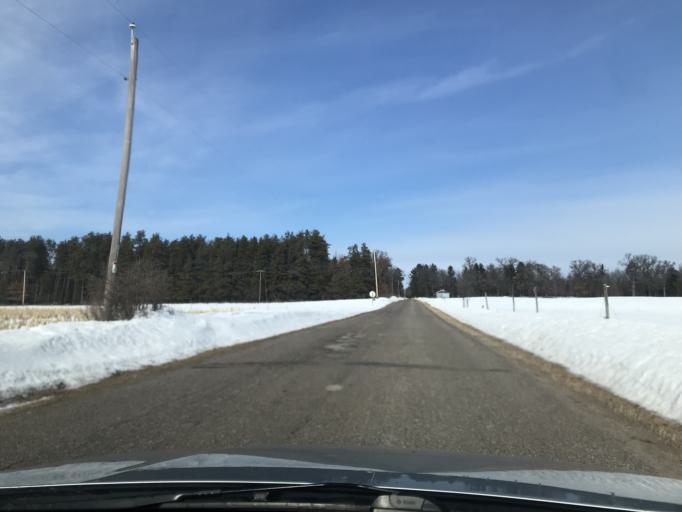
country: US
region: Wisconsin
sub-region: Marinette County
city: Peshtigo
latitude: 45.2194
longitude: -87.9628
